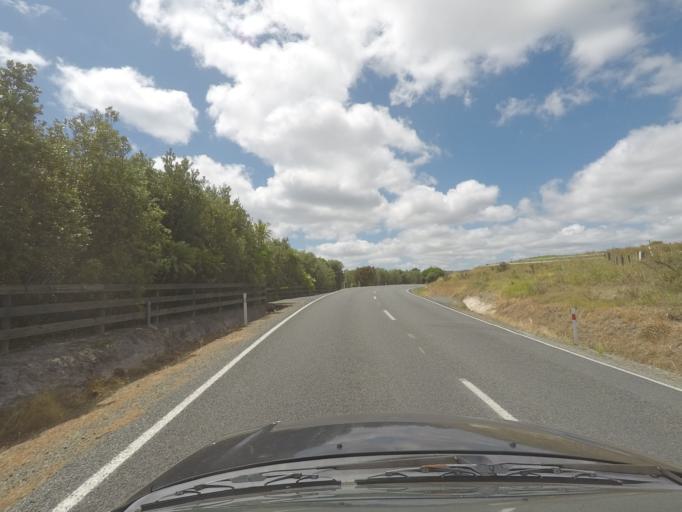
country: NZ
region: Northland
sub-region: Whangarei
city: Ruakaka
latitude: -36.0166
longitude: 174.4899
